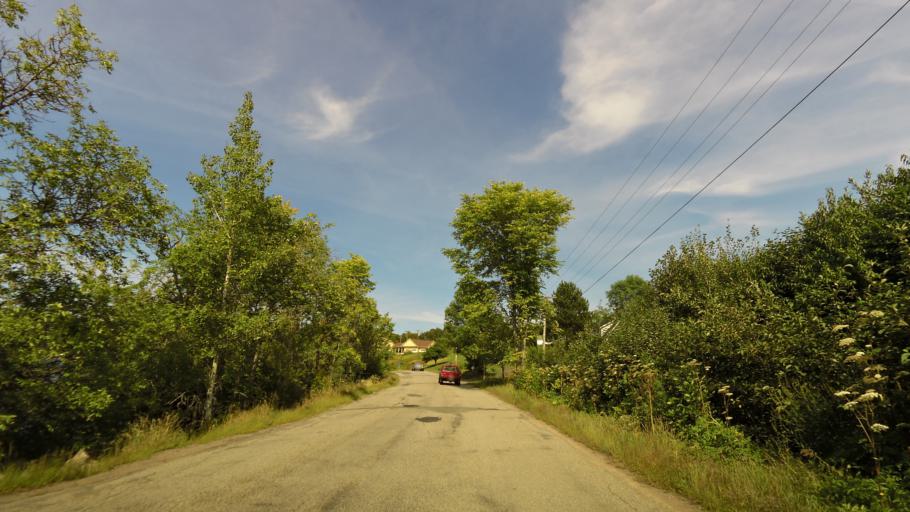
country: CA
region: New Brunswick
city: Hampton
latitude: 45.6062
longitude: -65.9061
